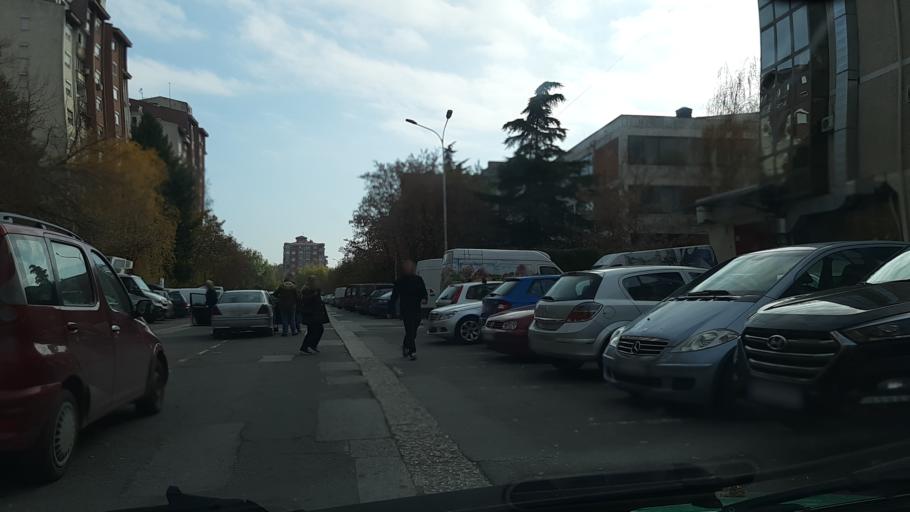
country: MK
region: Kisela Voda
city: Usje
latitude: 41.9846
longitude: 21.4693
